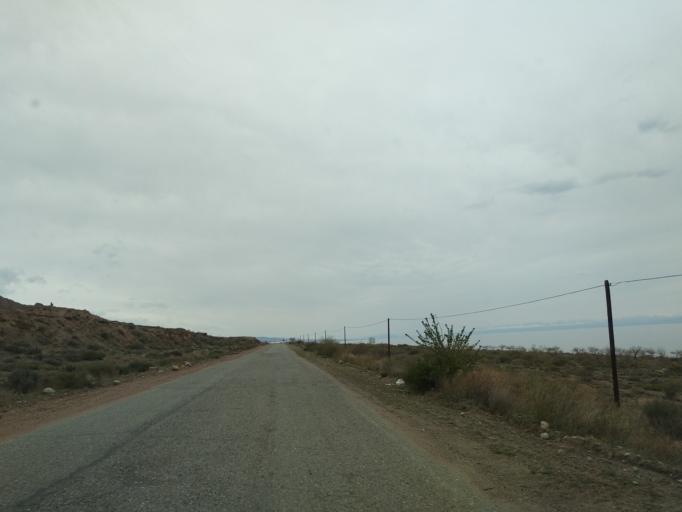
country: KG
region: Ysyk-Koel
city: Kadzhi-Say
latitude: 42.1722
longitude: 77.2568
